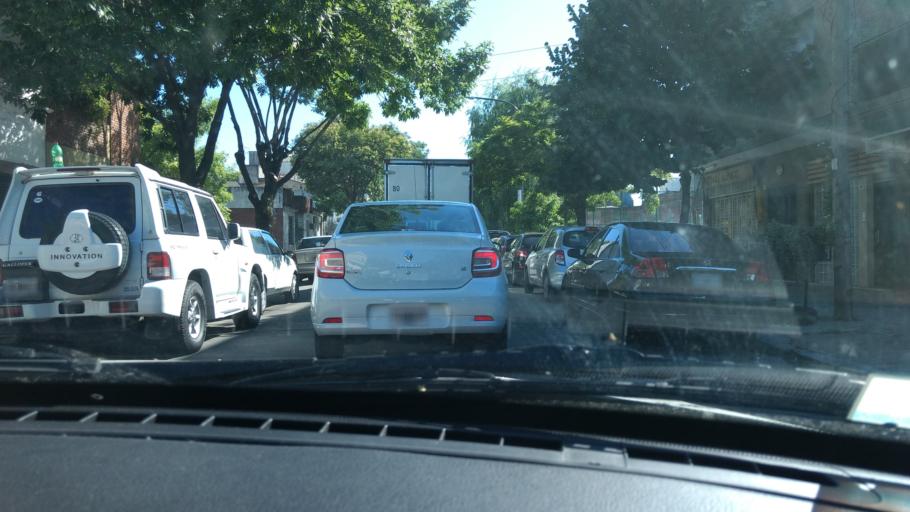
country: AR
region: Buenos Aires F.D.
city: Villa Santa Rita
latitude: -34.6168
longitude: -58.5148
